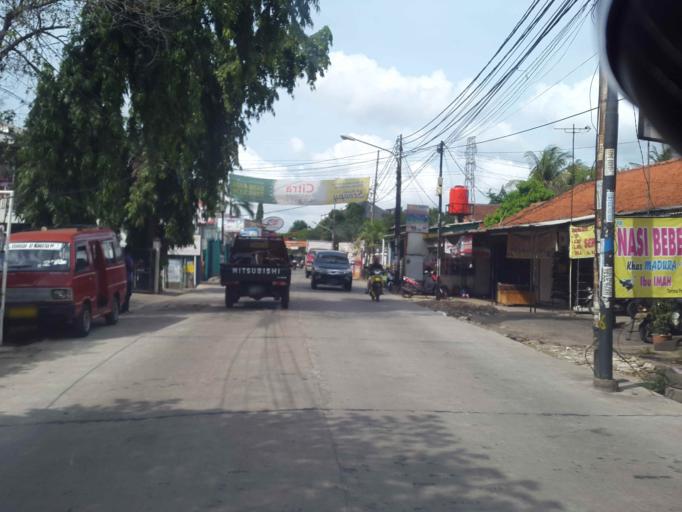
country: ID
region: West Java
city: Bekasi
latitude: -6.3016
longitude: 106.9238
